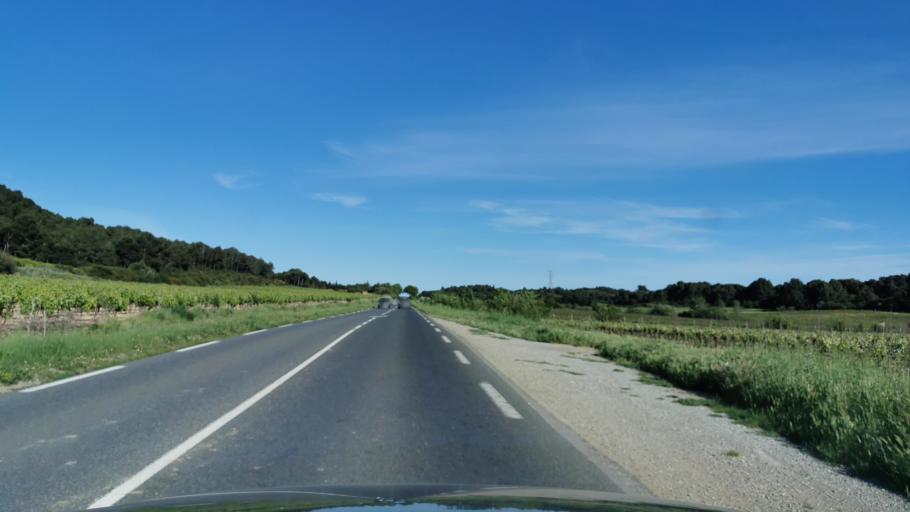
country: FR
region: Languedoc-Roussillon
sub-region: Departement de l'Aude
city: Moussan
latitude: 43.2099
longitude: 2.9467
